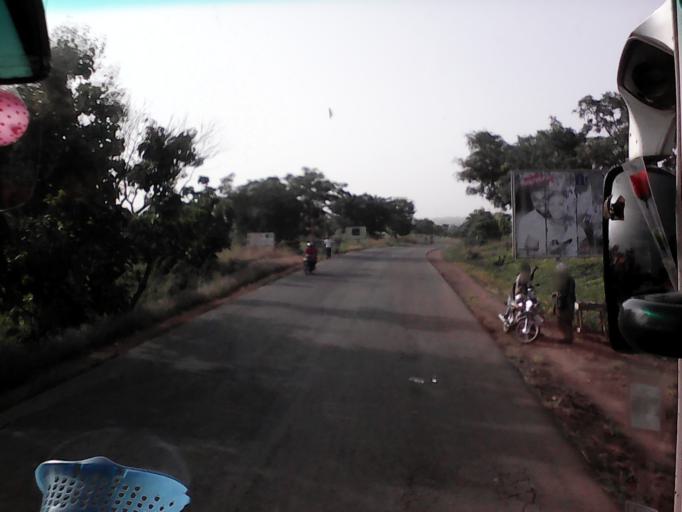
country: TG
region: Kara
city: Kara
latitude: 9.5173
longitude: 1.2091
